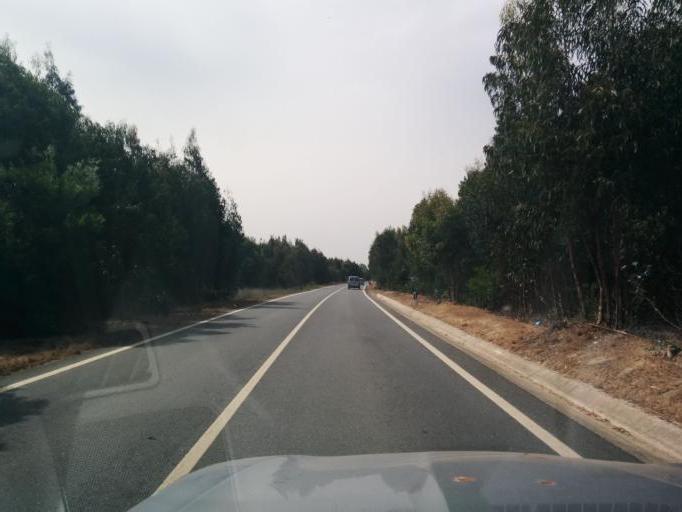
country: PT
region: Beja
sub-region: Odemira
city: Vila Nova de Milfontes
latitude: 37.6706
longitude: -8.7596
